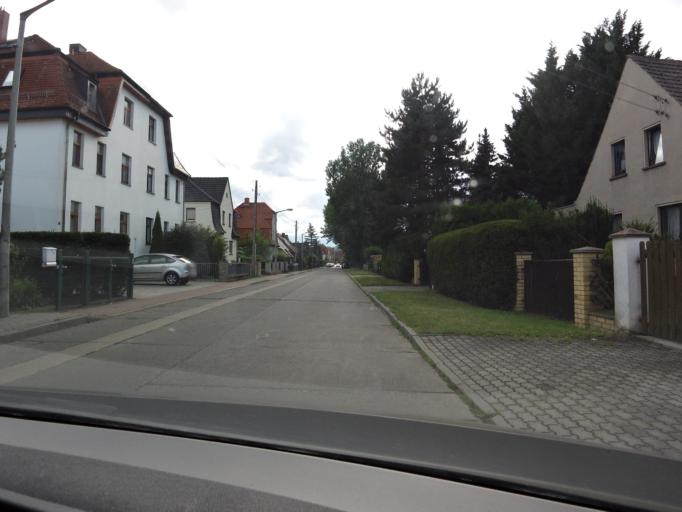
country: DE
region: Saxony
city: Markranstadt
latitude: 51.3036
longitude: 12.2655
